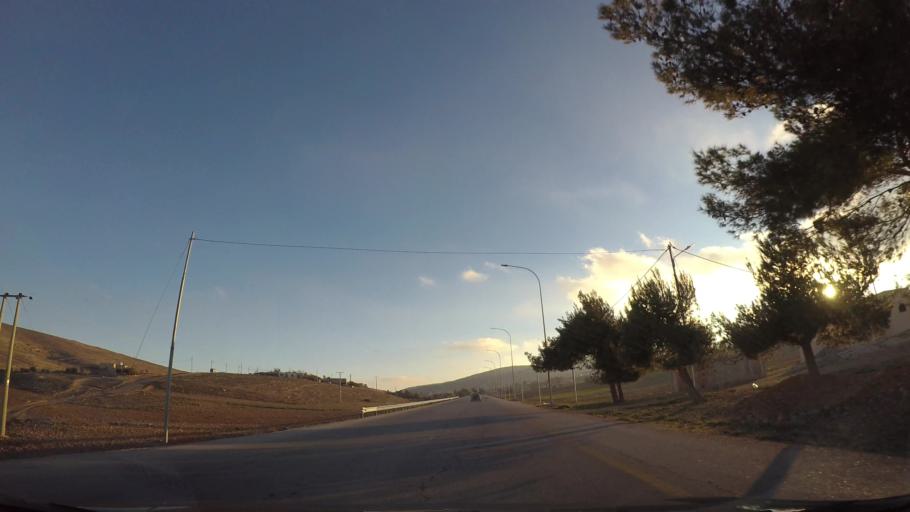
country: JO
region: Ma'an
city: Petra
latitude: 30.4439
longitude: 35.5216
